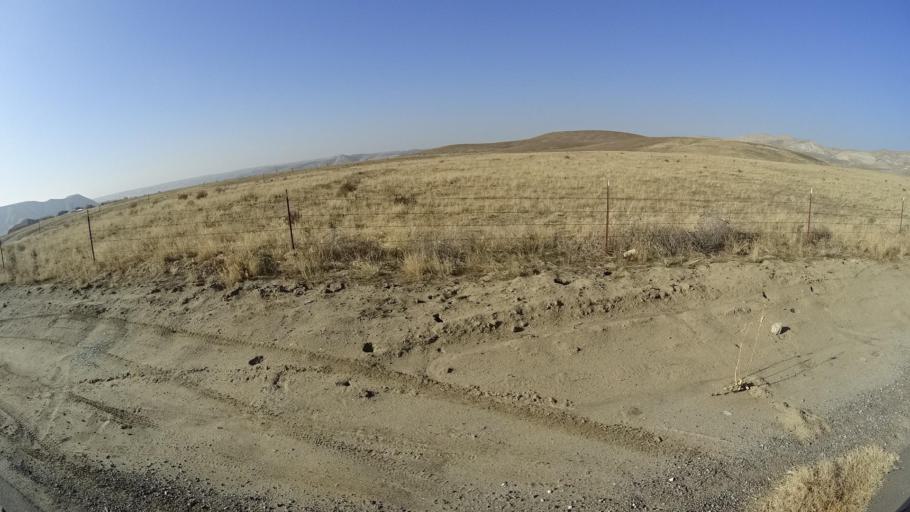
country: US
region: California
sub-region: Kern County
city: Oildale
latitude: 35.4473
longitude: -118.8855
